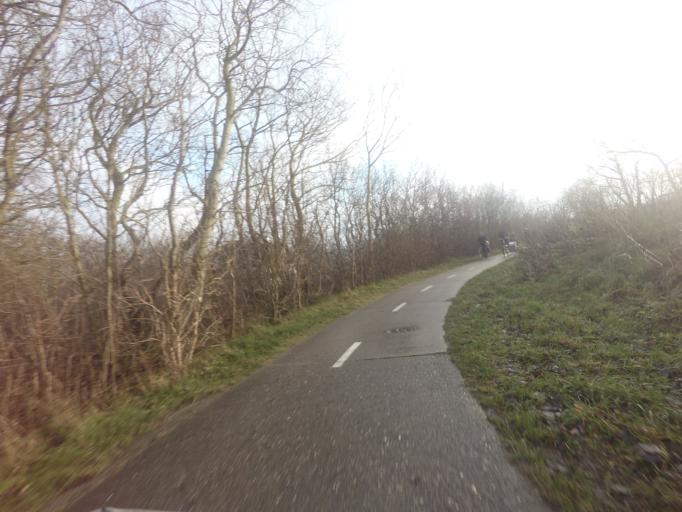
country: NL
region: North Holland
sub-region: Gemeente Texel
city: Den Burg
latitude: 53.1555
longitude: 4.8464
